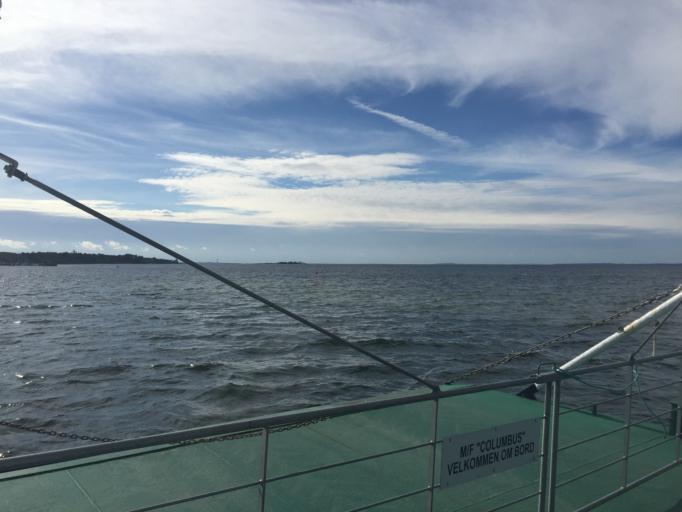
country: DK
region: Capital Region
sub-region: Halsnaes Kommune
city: Hundested
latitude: 55.9429
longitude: 11.9037
